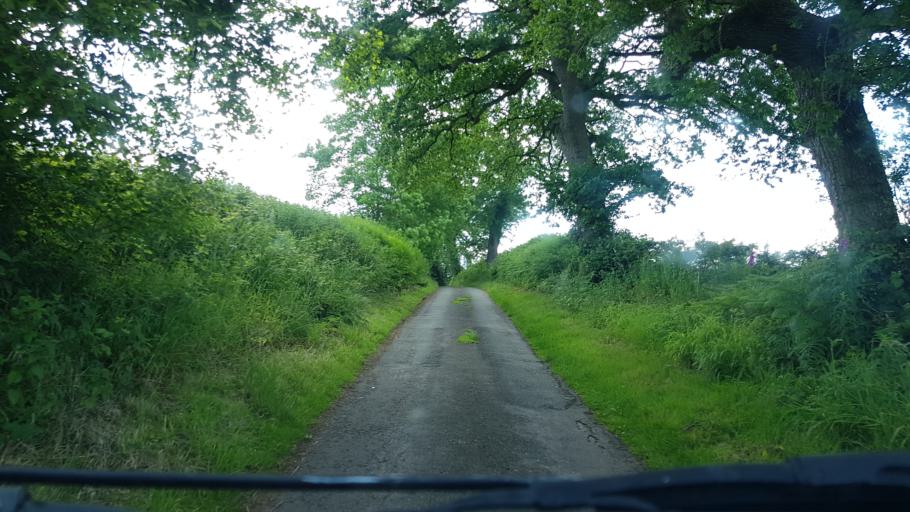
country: GB
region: England
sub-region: Shropshire
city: Romsley
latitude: 52.4622
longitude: -2.2819
